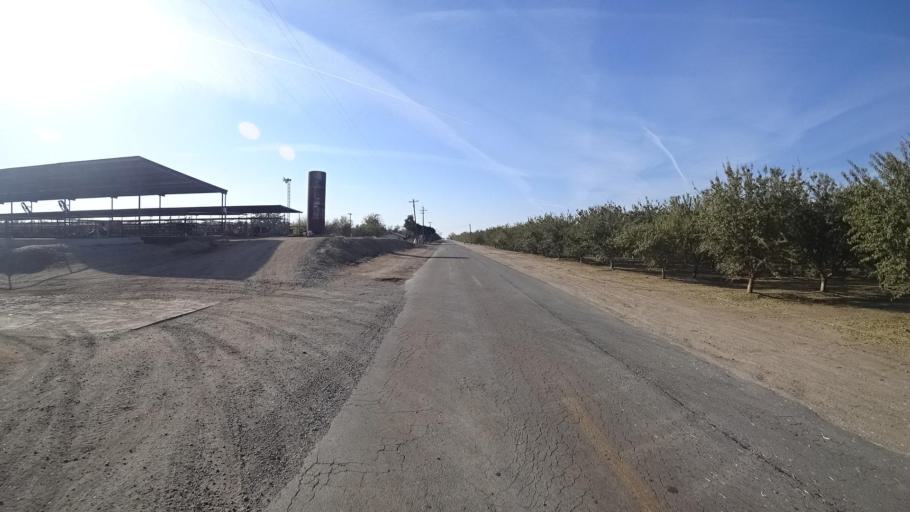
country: US
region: California
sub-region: Kern County
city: McFarland
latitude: 35.7033
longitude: -119.2532
